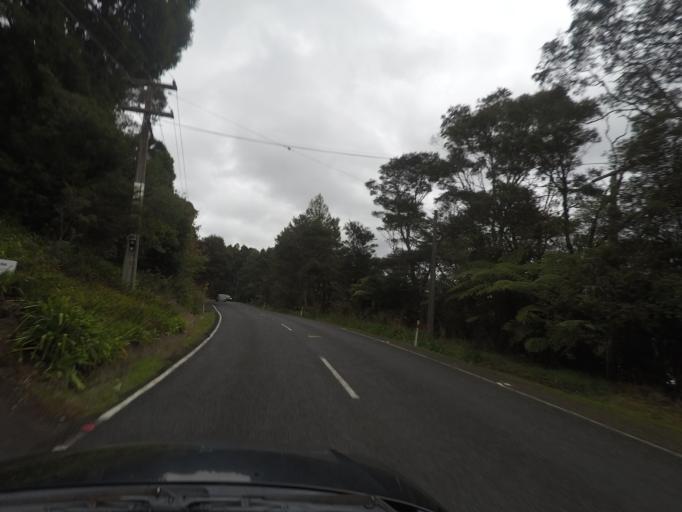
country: NZ
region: Auckland
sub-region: Auckland
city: Titirangi
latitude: -36.9226
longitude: 174.6021
